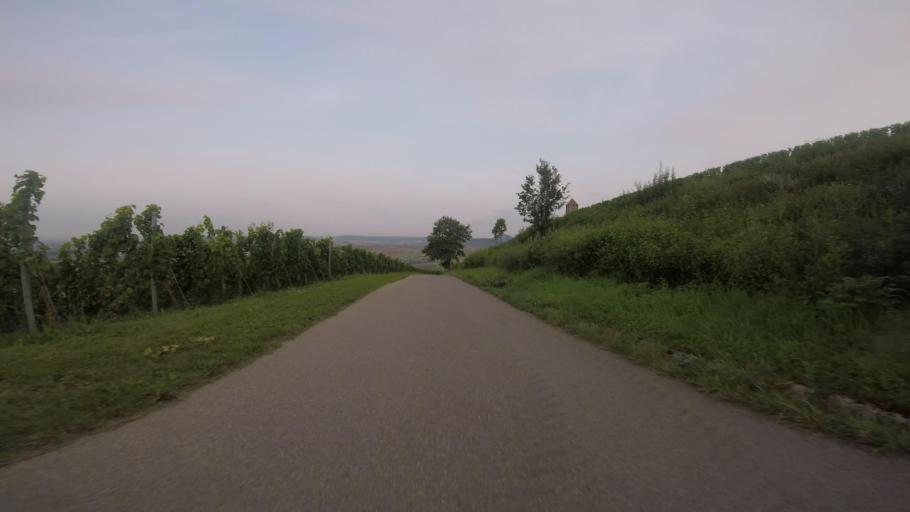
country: DE
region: Baden-Wuerttemberg
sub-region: Regierungsbezirk Stuttgart
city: Oberstenfeld
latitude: 49.0117
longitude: 9.3307
